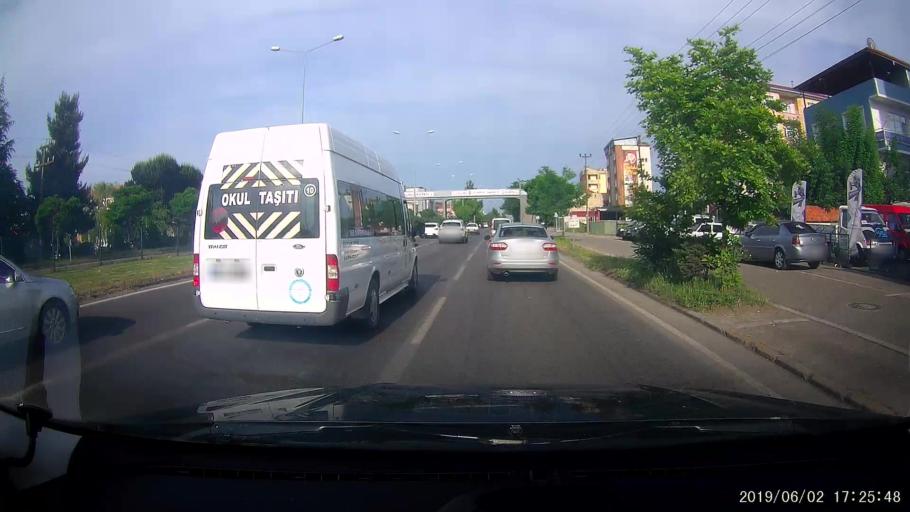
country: TR
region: Samsun
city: Carsamba
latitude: 41.2046
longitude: 36.7117
